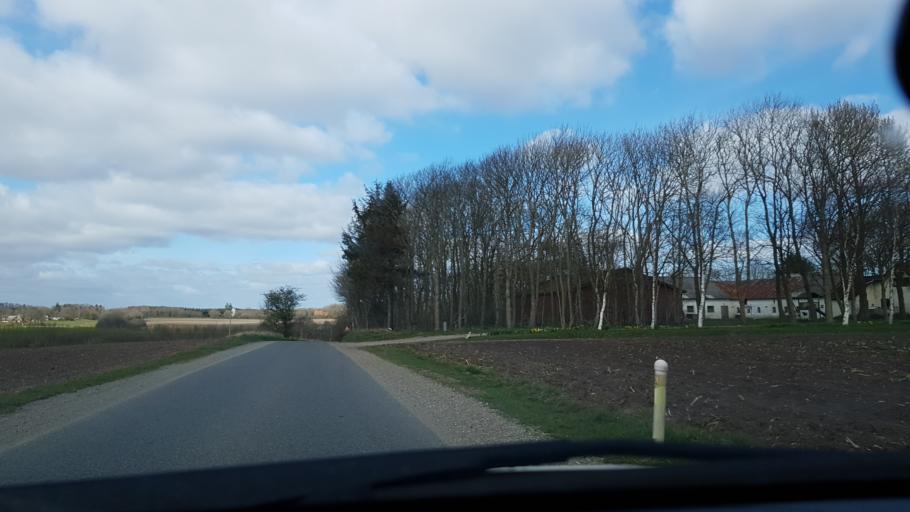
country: DK
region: South Denmark
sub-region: Vejen Kommune
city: Rodding
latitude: 55.3749
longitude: 8.9972
